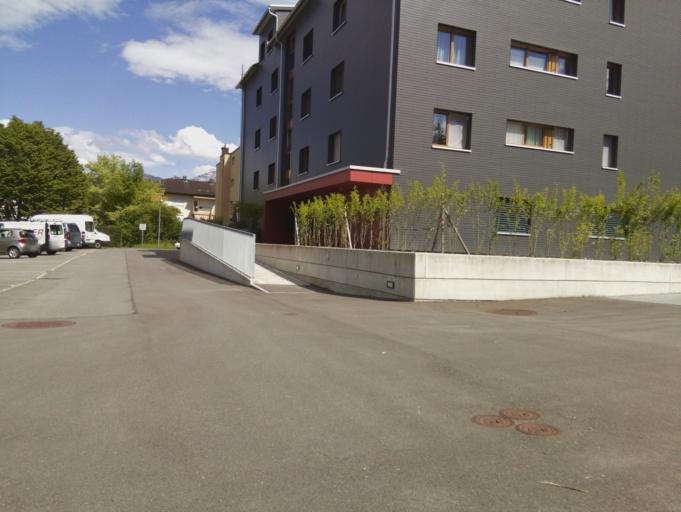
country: CH
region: Schwyz
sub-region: Bezirk March
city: Schubelbach
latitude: 47.1750
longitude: 8.9400
